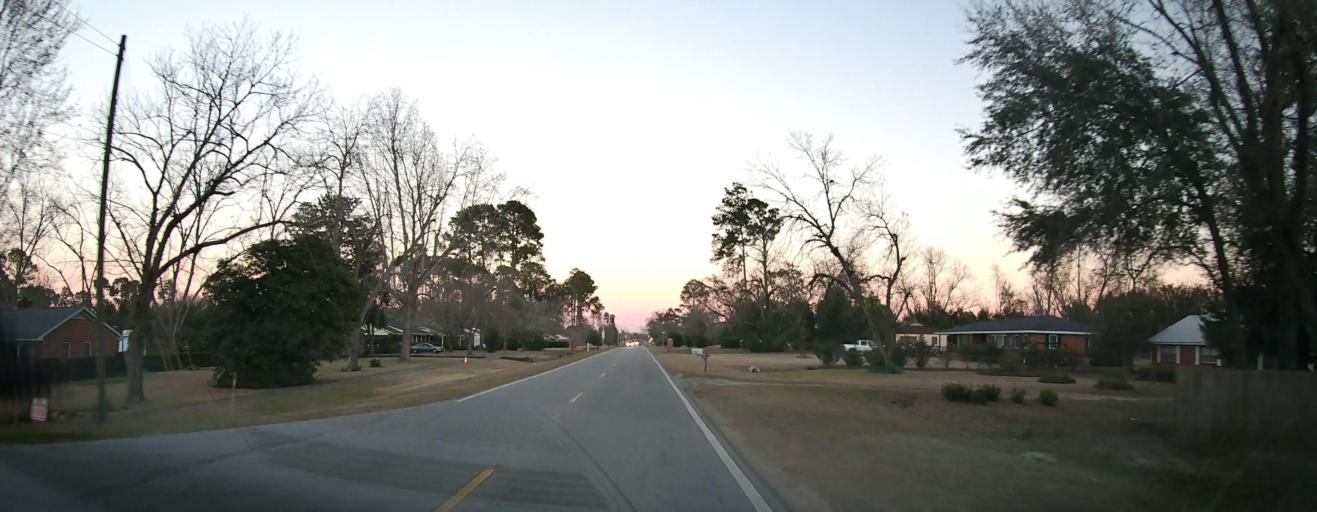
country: US
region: Georgia
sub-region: Dougherty County
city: Albany
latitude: 31.5293
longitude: -84.1273
